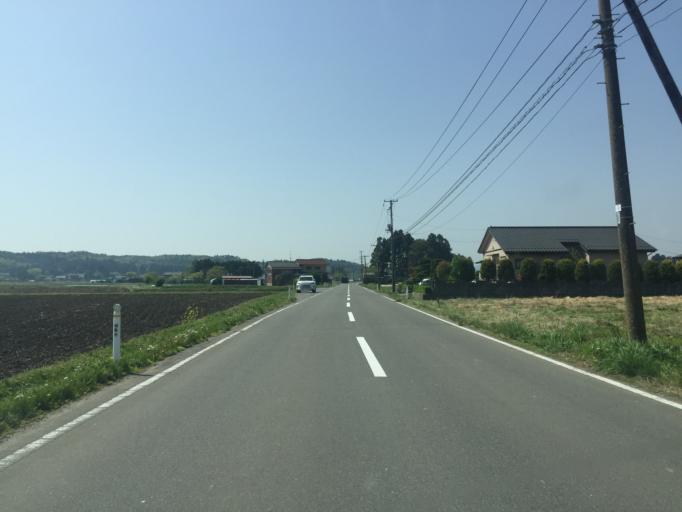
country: JP
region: Miyagi
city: Marumori
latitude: 37.7748
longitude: 140.9561
